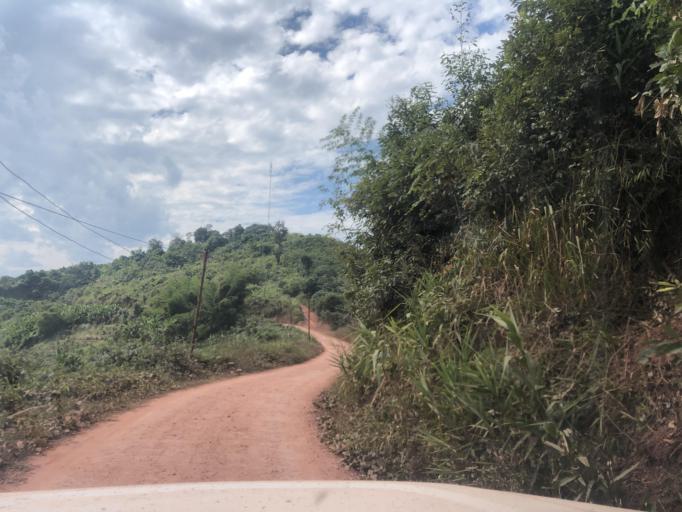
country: CN
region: Yunnan
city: Menglie
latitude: 22.1247
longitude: 101.7409
